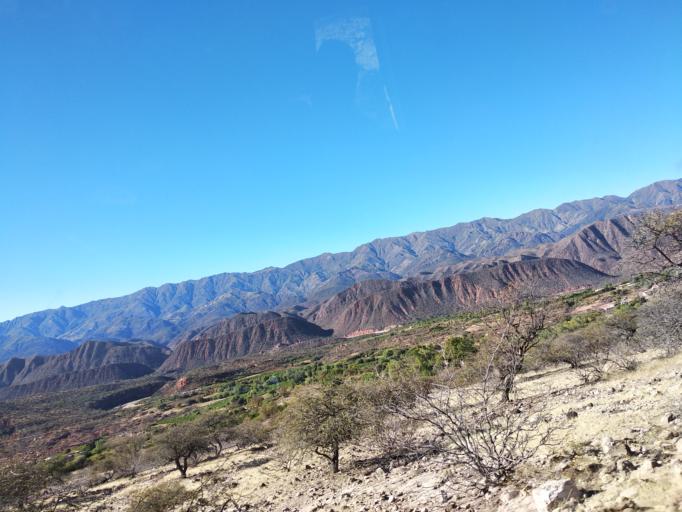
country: BO
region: Cochabamba
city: Mizque
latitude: -18.0826
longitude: -65.7471
